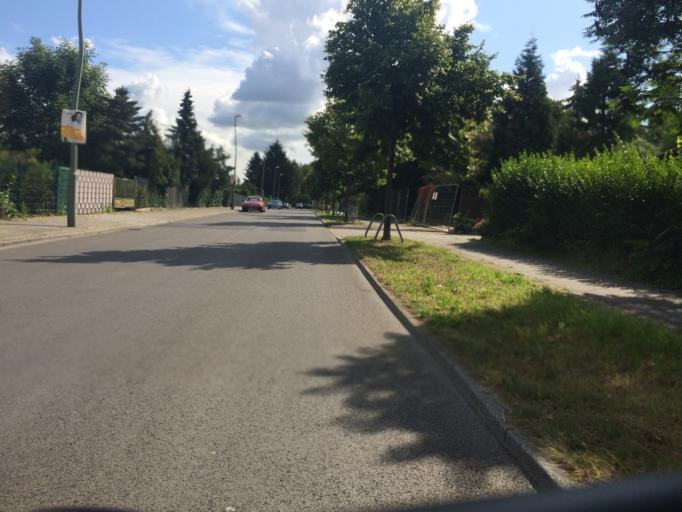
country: DE
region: Berlin
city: Heinersdorf
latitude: 52.5679
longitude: 13.4514
